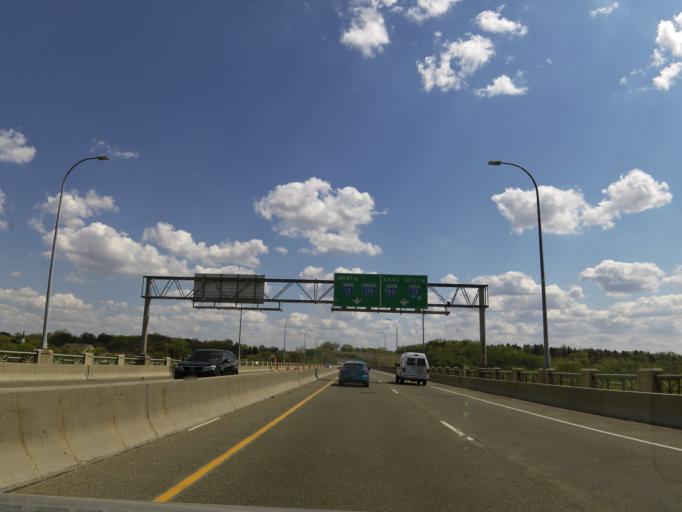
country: US
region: Minnesota
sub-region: Dakota County
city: Mendota Heights
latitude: 44.8864
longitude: -93.1762
